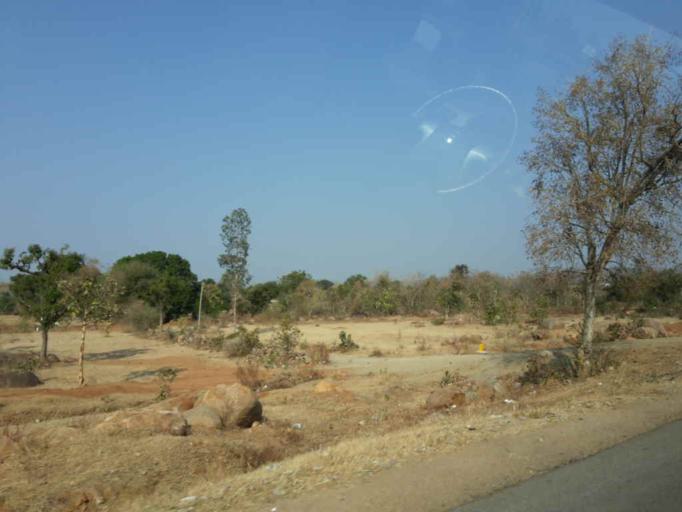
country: IN
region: Telangana
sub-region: Nizamabad District
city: Nizamabad
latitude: 18.5251
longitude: 78.2332
